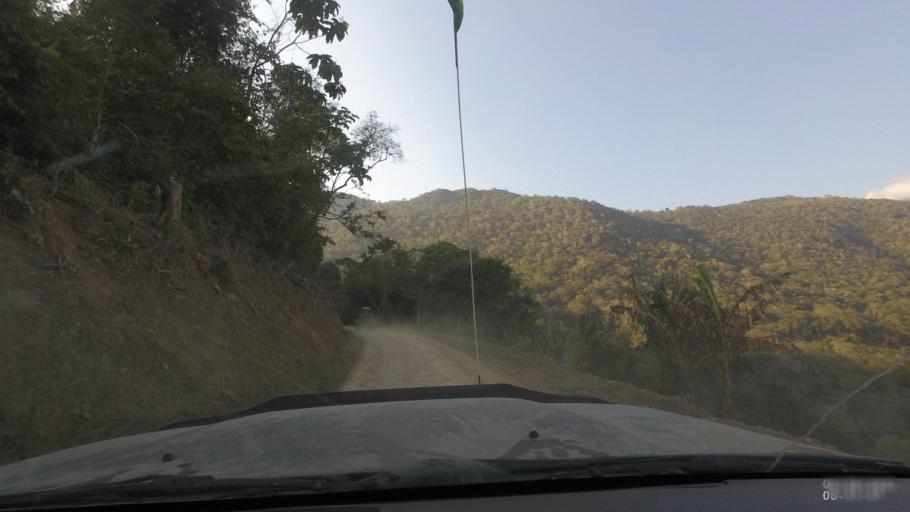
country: BO
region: La Paz
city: Quime
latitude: -16.5051
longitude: -66.7623
